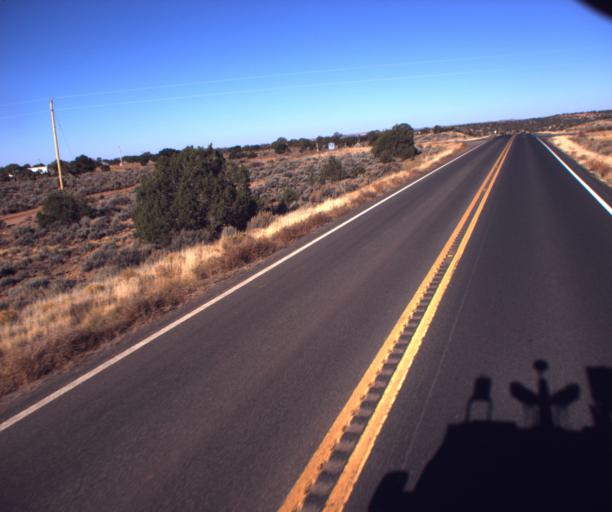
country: US
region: Arizona
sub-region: Apache County
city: Ganado
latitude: 35.7651
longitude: -109.7888
